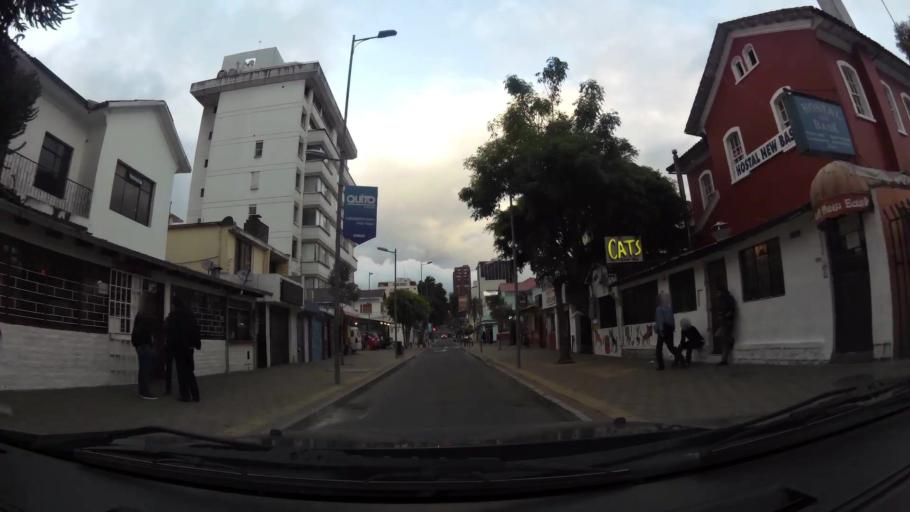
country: EC
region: Pichincha
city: Quito
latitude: -0.2026
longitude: -78.4898
